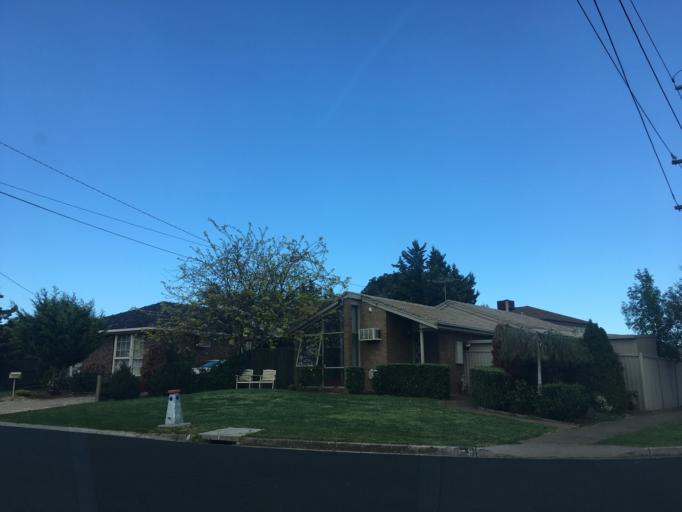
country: AU
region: Victoria
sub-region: Wyndham
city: Hoppers Crossing
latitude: -37.8701
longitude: 144.7058
